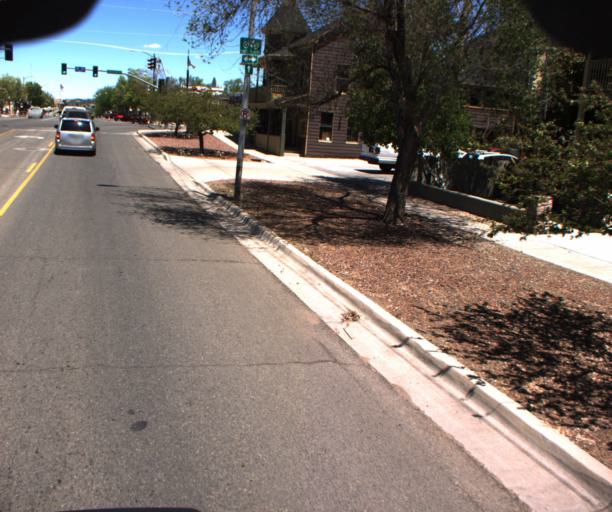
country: US
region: Arizona
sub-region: Yavapai County
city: Prescott
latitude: 34.5374
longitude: -112.4702
